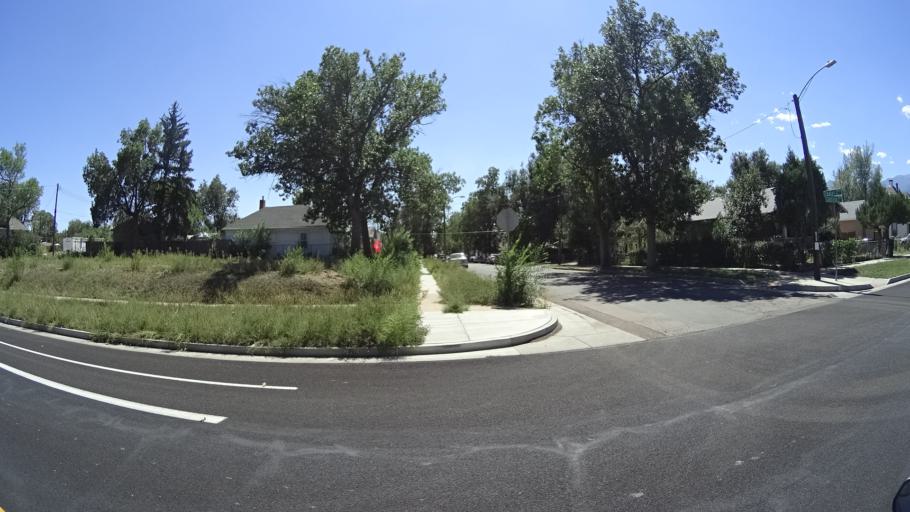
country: US
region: Colorado
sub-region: El Paso County
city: Colorado Springs
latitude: 38.8277
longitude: -104.8056
